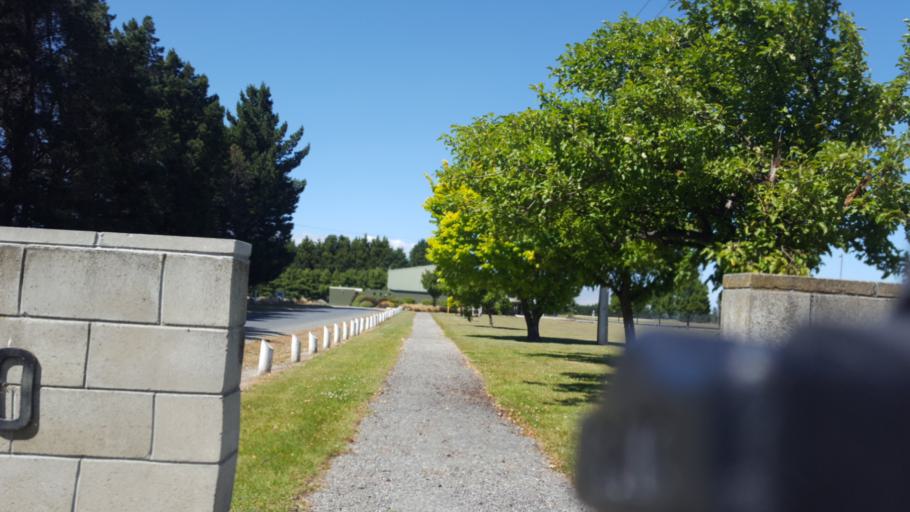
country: NZ
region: Otago
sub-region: Dunedin City
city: Dunedin
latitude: -45.1311
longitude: 170.1059
